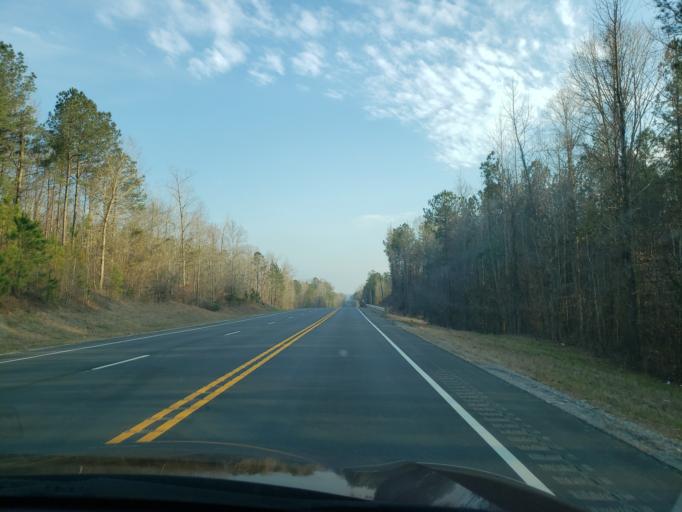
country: US
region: Alabama
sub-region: Hale County
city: Moundville
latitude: 32.8530
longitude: -87.6125
